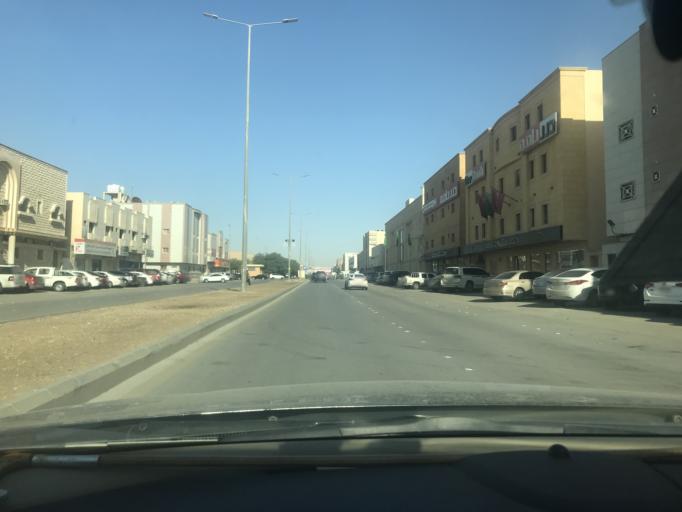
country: SA
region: Ar Riyad
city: Riyadh
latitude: 24.7522
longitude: 46.6699
